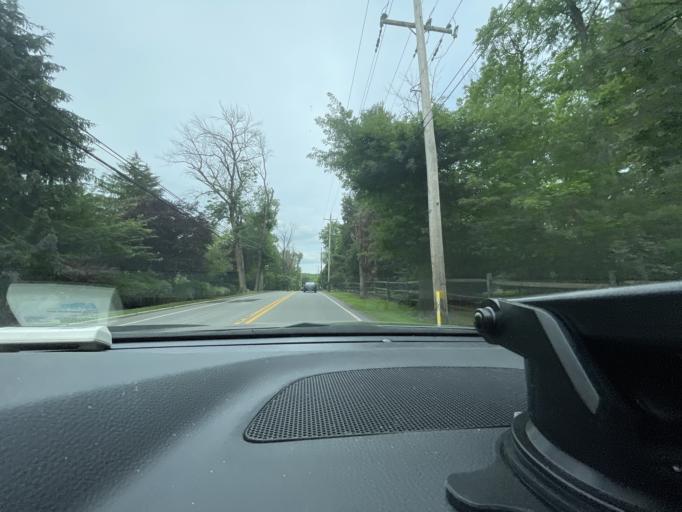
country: US
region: Pennsylvania
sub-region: Montgomery County
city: Blue Bell
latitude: 40.1644
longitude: -75.2604
